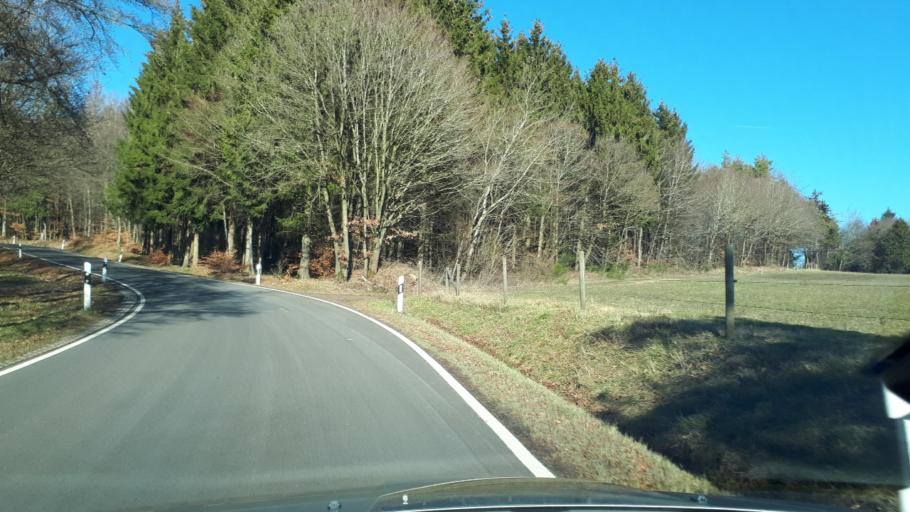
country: DE
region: Rheinland-Pfalz
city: Ellscheid
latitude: 50.1573
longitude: 6.9188
